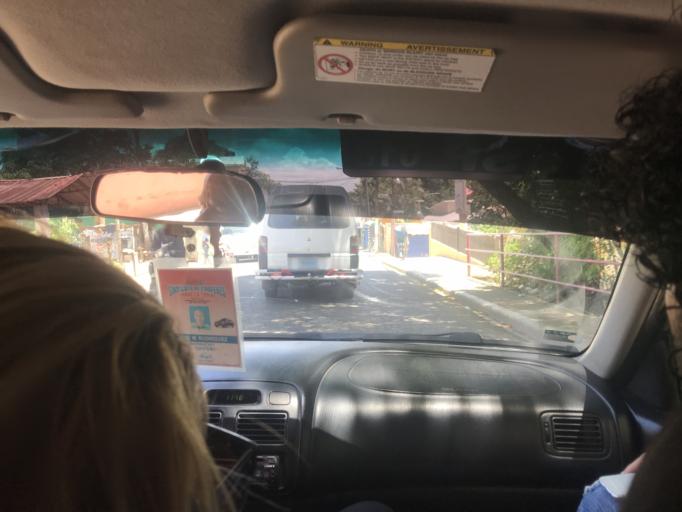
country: DO
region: Santiago
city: Santiago de los Caballeros
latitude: 19.4113
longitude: -70.6734
